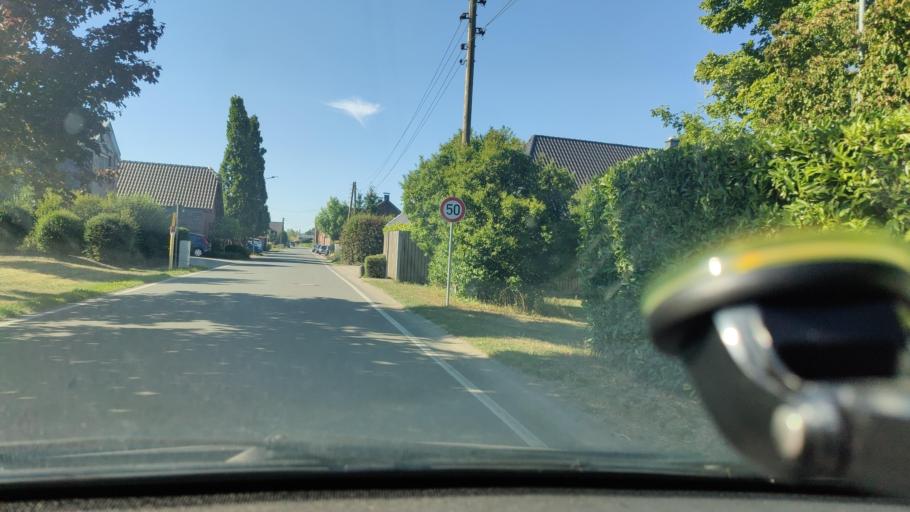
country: DE
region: North Rhine-Westphalia
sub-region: Regierungsbezirk Dusseldorf
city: Wachtendonk
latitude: 51.4638
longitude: 6.3579
